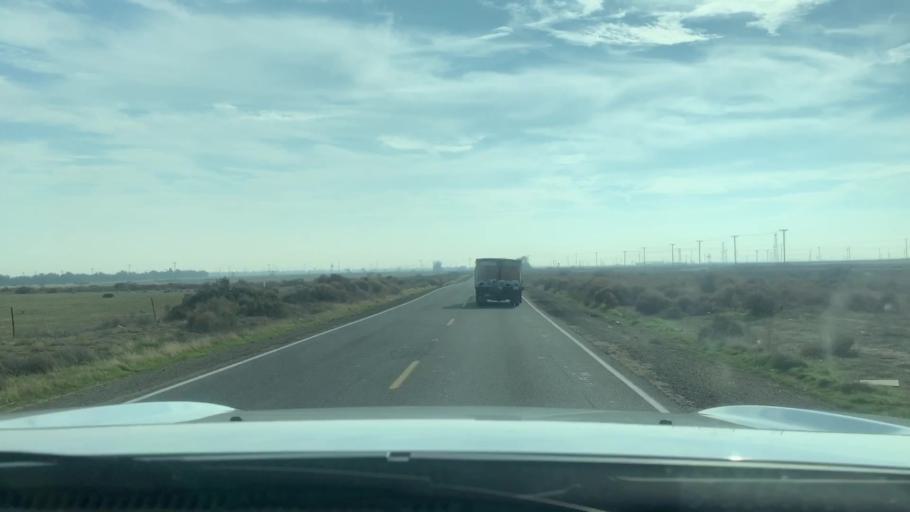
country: US
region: California
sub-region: Kern County
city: Lost Hills
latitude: 35.5472
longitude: -119.7844
